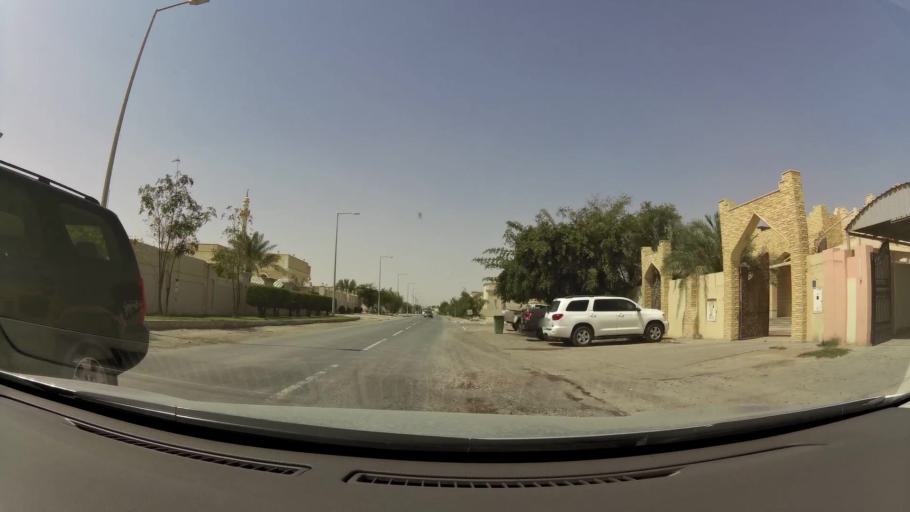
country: QA
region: Baladiyat Umm Salal
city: Umm Salal Muhammad
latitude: 25.3767
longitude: 51.4261
